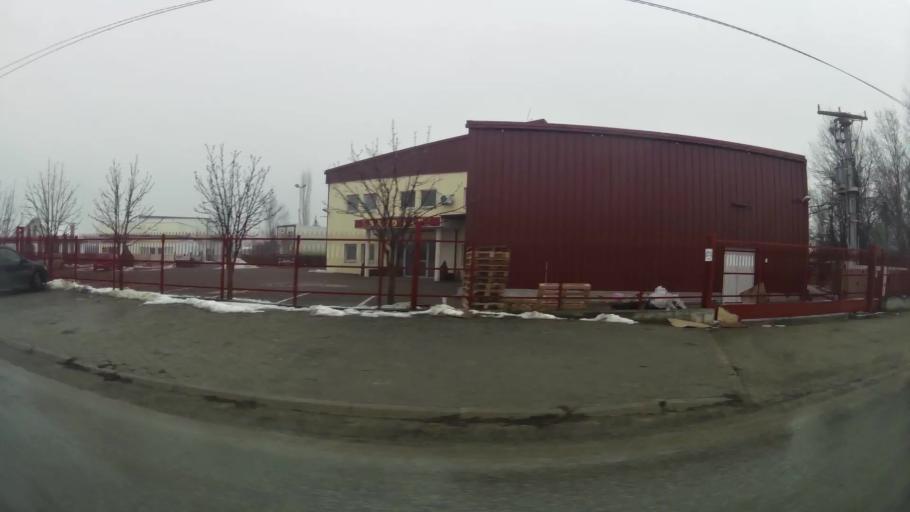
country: MK
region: Ilinden
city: Idrizovo
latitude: 41.9502
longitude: 21.5869
